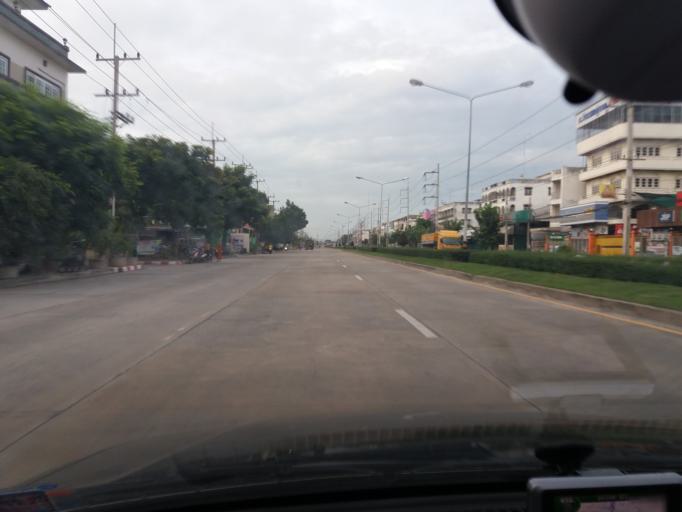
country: TH
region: Suphan Buri
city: U Thong
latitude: 14.3837
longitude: 99.8947
